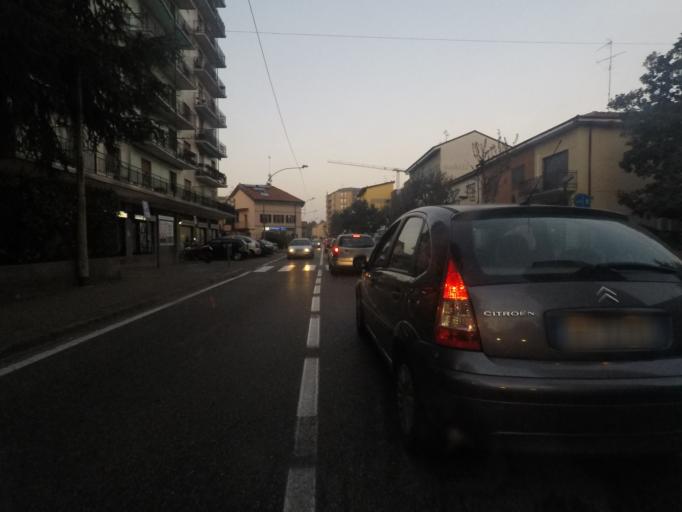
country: IT
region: Lombardy
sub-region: Citta metropolitana di Milano
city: Cologno Monzese
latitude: 45.5275
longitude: 9.2778
